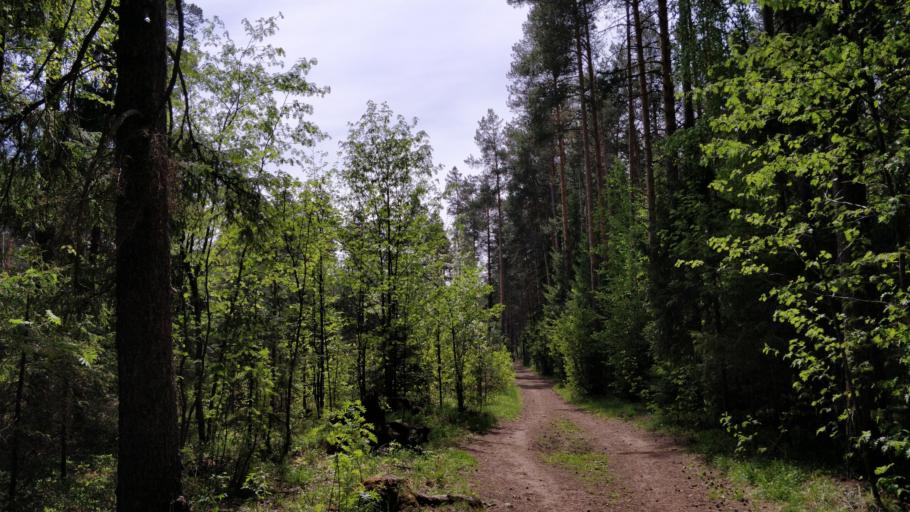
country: RU
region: Perm
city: Kondratovo
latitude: 57.9843
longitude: 56.1376
